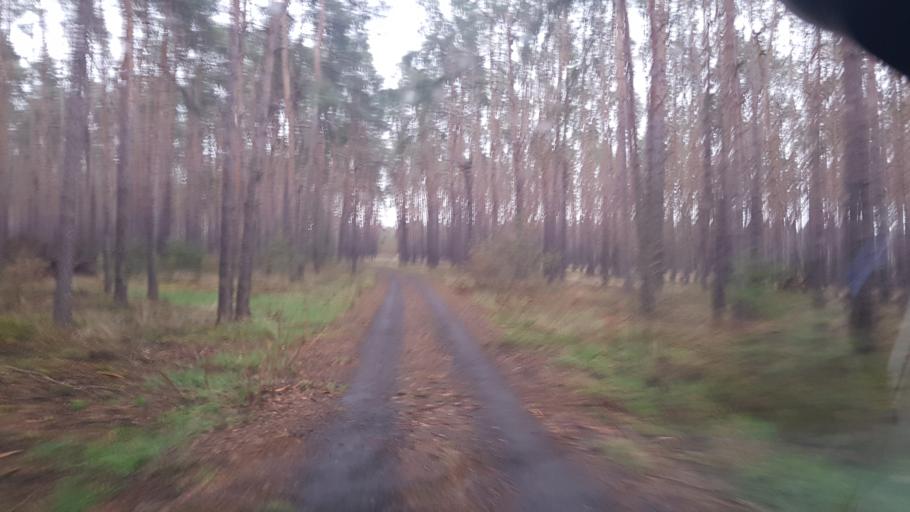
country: DE
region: Brandenburg
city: Muhlberg
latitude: 51.4969
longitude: 13.2961
